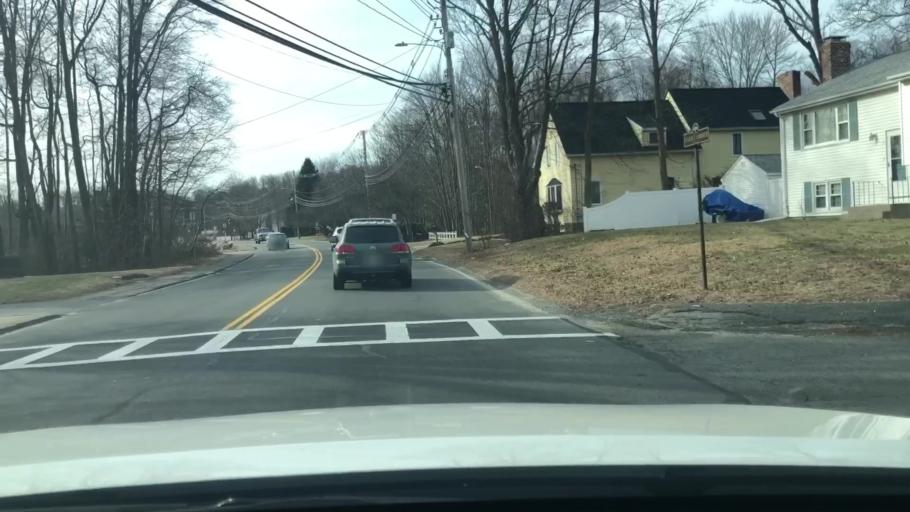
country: US
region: Massachusetts
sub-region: Worcester County
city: Milford
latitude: 42.1513
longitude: -71.5312
